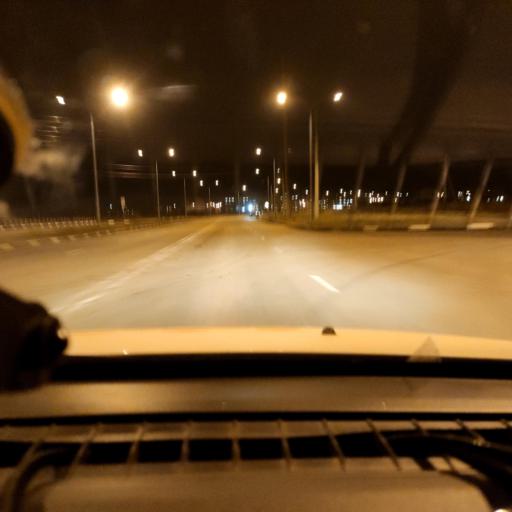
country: RU
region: Samara
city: Samara
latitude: 53.1429
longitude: 50.0775
